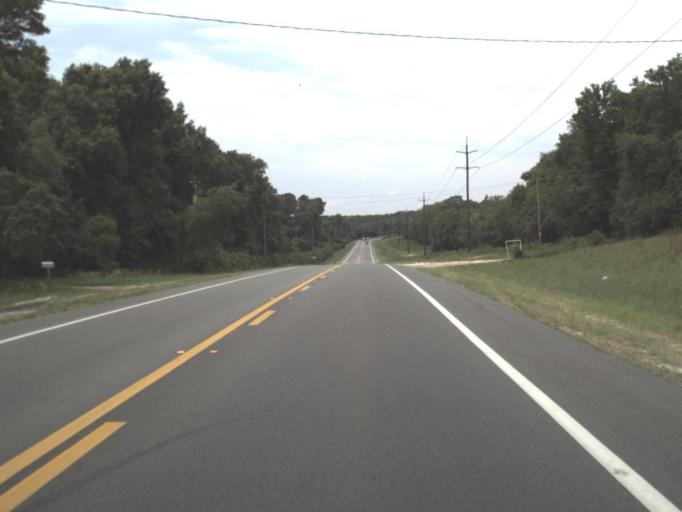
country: US
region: Florida
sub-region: Putnam County
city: Interlachen
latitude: 29.6199
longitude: -81.9689
